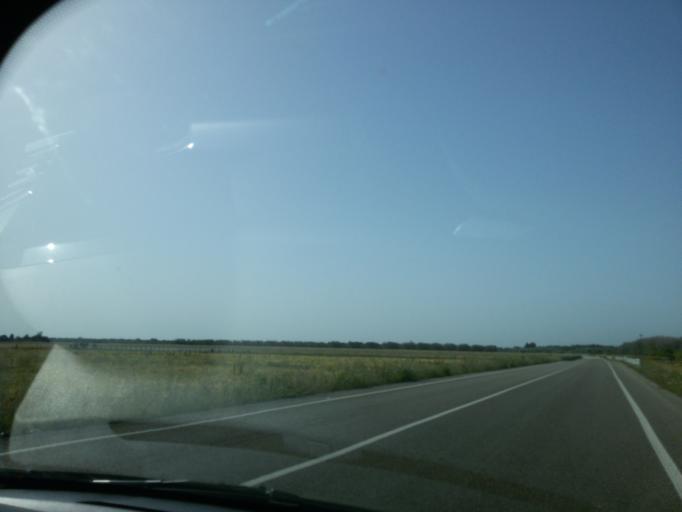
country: IT
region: Apulia
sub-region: Provincia di Brindisi
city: Mesagne
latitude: 40.4999
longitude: 17.8284
